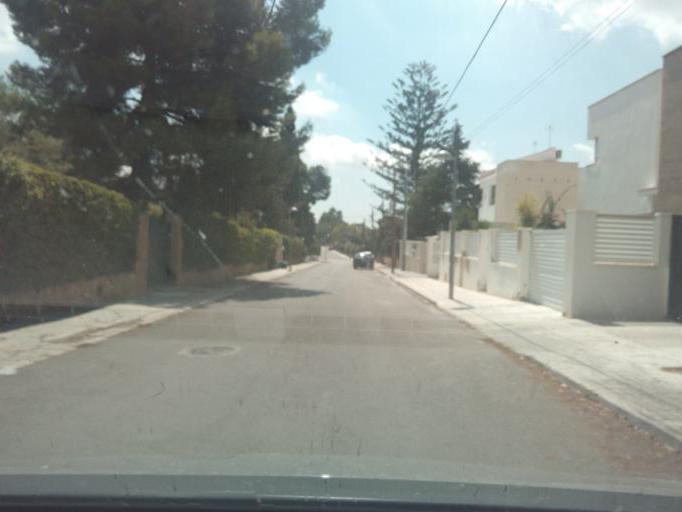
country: ES
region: Valencia
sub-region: Provincia de Valencia
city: L'Eliana
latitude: 39.5403
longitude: -0.4864
